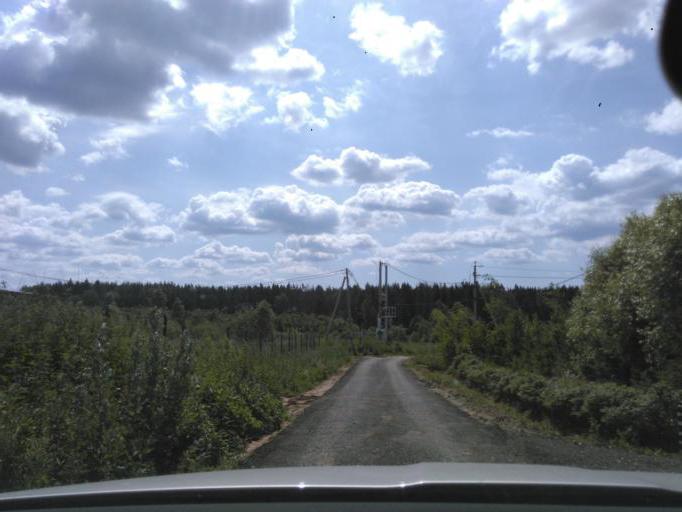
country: RU
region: Moskovskaya
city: Solnechnogorsk
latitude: 56.1275
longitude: 36.9672
